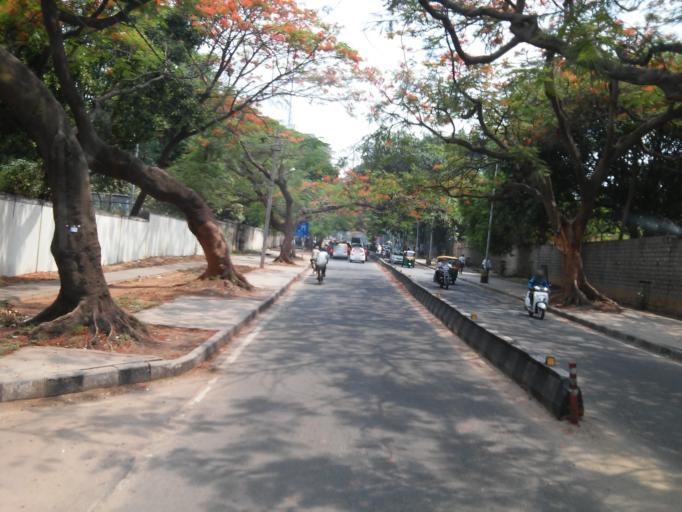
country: IN
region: Karnataka
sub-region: Bangalore Urban
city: Bangalore
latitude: 12.9775
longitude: 77.6151
